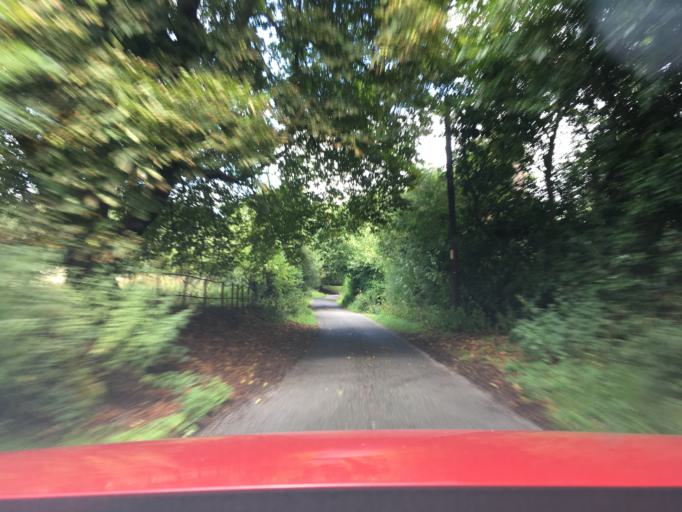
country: GB
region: England
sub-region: West Berkshire
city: Welford
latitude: 51.4172
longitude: -1.3993
